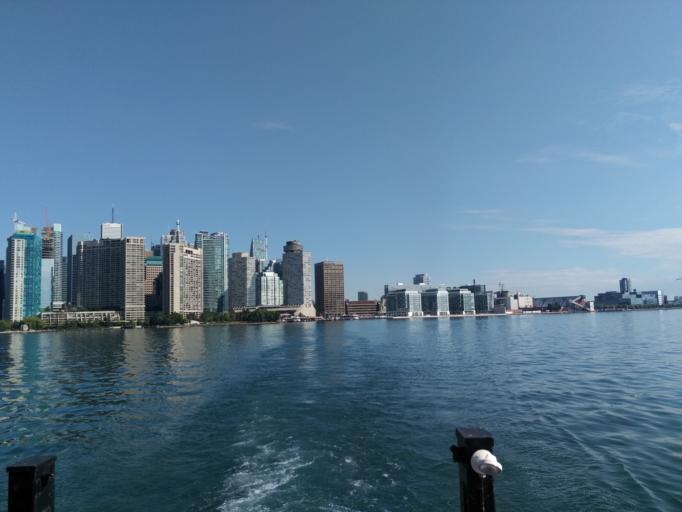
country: CA
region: Ontario
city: Toronto
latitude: 43.6331
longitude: -79.3754
